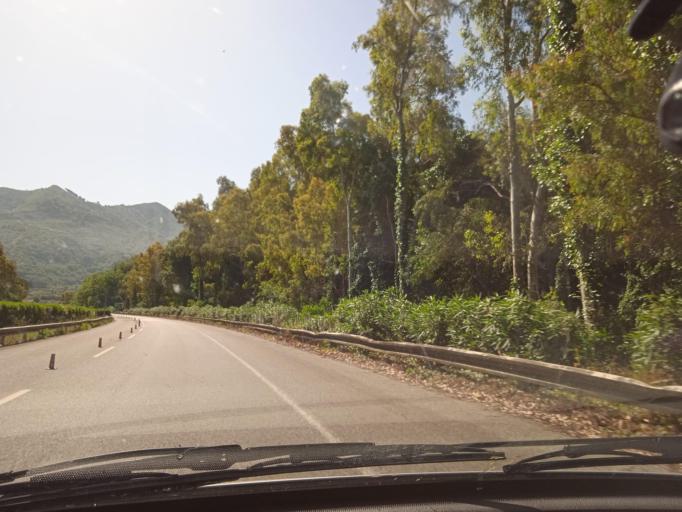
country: IT
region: Sicily
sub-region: Messina
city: Piraino
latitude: 38.1409
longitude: 14.8661
